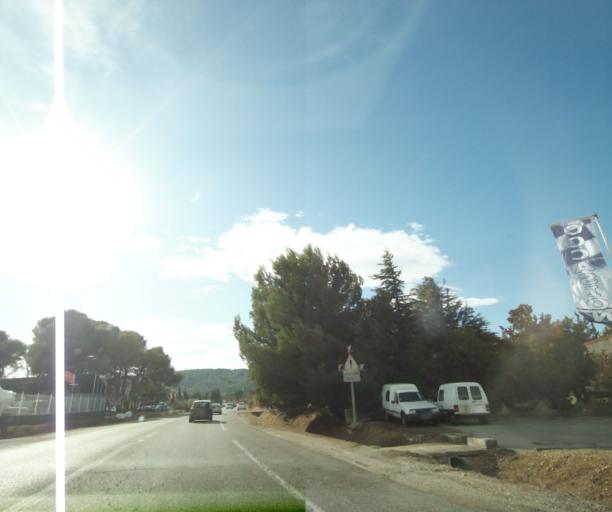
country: FR
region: Provence-Alpes-Cote d'Azur
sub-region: Departement des Bouches-du-Rhone
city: Chateauneuf-les-Martigues
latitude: 43.3804
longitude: 5.1912
